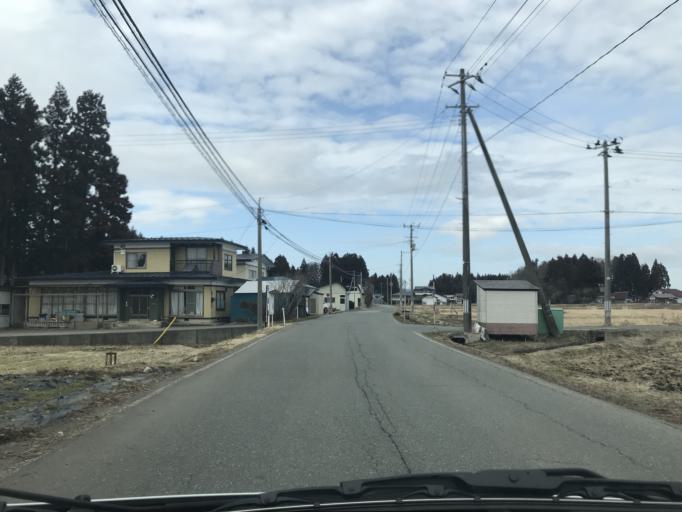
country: JP
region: Iwate
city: Kitakami
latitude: 39.3258
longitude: 140.9854
